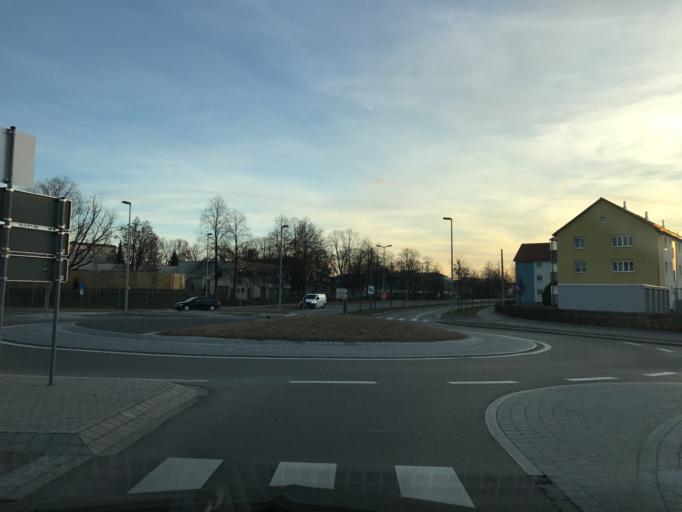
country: DE
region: Baden-Wuerttemberg
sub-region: Tuebingen Region
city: Friedrichshafen
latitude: 47.6622
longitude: 9.4918
